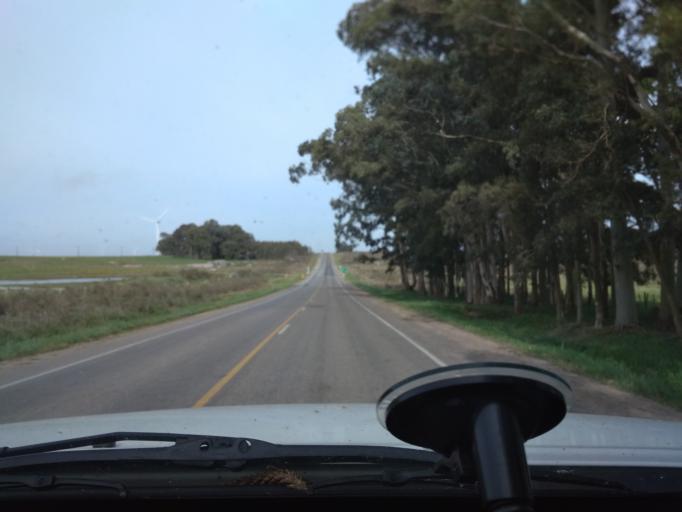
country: UY
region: Florida
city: Florida
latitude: -34.0677
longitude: -56.0598
